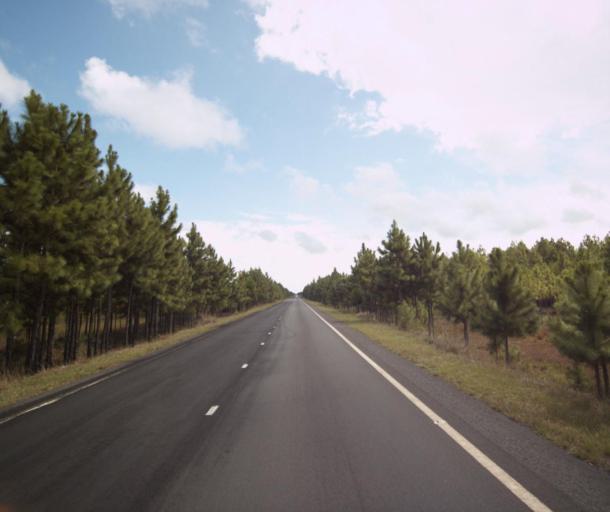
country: BR
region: Rio Grande do Sul
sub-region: Tapes
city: Tapes
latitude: -31.4153
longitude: -51.1734
